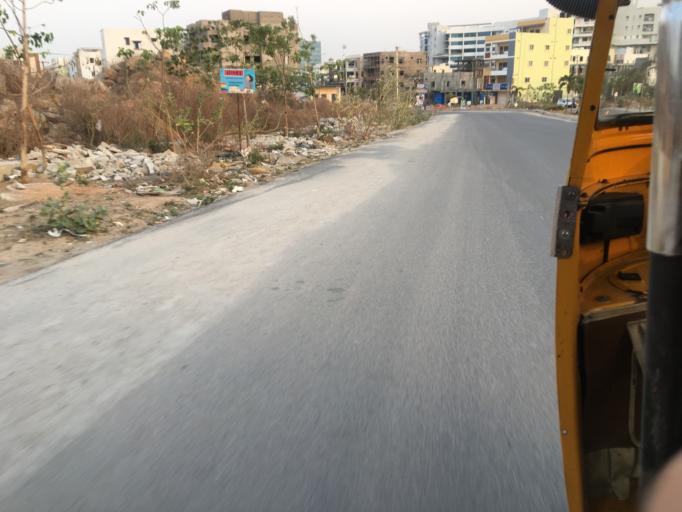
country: IN
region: Telangana
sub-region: Medak
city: Serilingampalle
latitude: 17.4305
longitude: 78.3313
